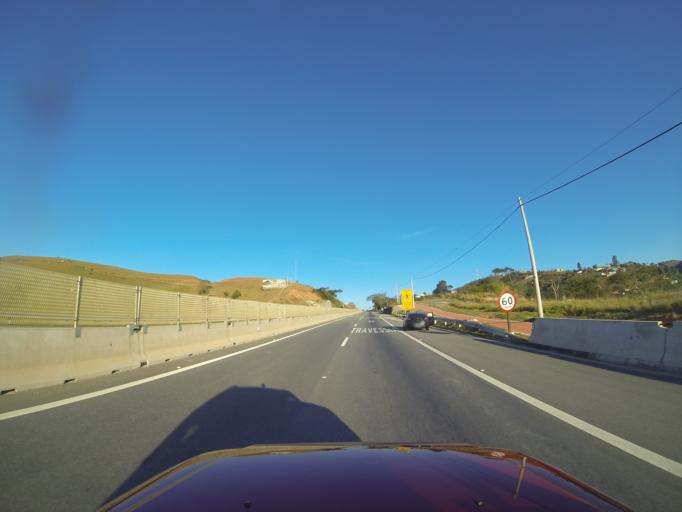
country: BR
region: Sao Paulo
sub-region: Santa Branca
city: Santa Branca
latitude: -23.3660
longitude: -45.6826
